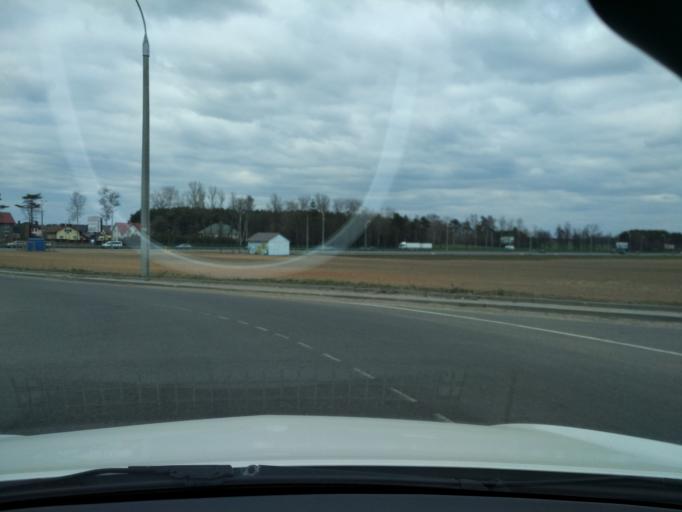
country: BY
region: Minsk
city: Bal'shavik
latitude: 53.9688
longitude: 27.5513
